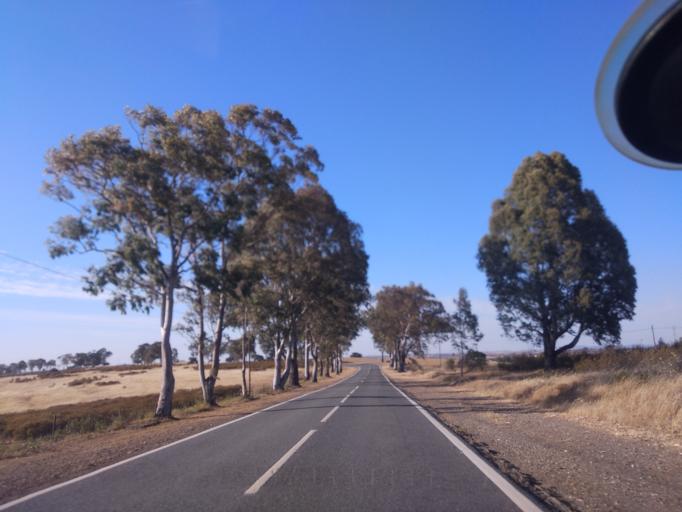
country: PT
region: Beja
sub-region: Almodovar
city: Almodovar
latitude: 37.4499
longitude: -7.9966
